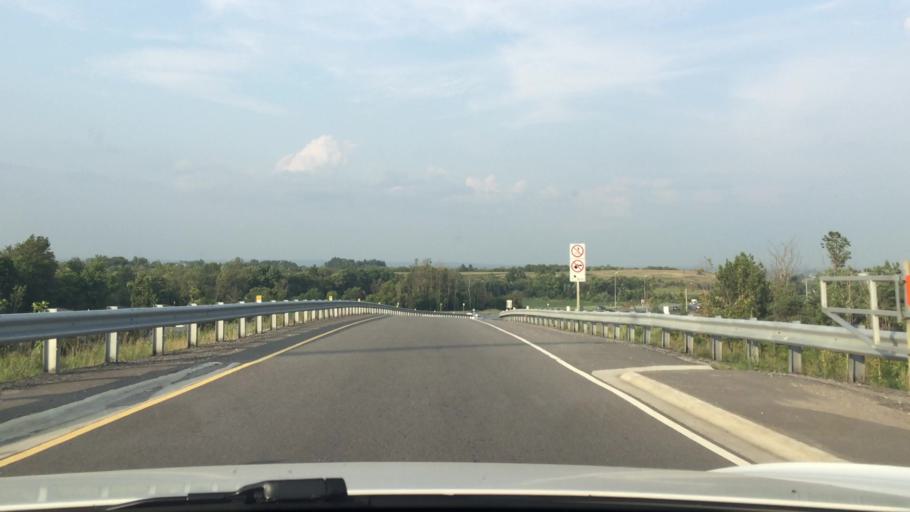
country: CA
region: Ontario
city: Oshawa
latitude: 43.8832
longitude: -78.7215
